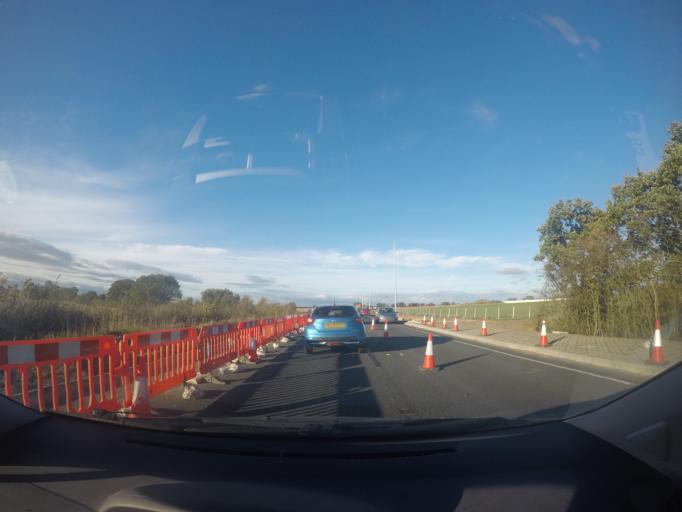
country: GB
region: England
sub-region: City of York
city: Nether Poppleton
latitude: 53.9535
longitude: -1.1490
